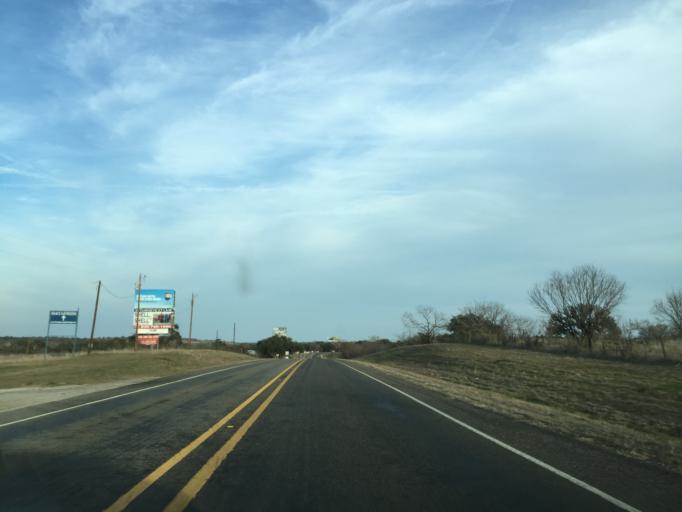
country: US
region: Texas
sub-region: Llano County
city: Llano
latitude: 30.7617
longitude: -98.6356
